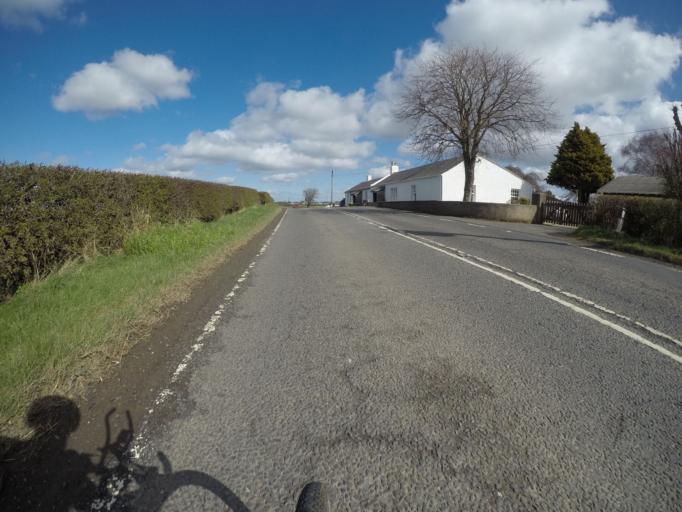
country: GB
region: Scotland
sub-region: East Ayrshire
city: Crosshouse
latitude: 55.5892
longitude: -4.5547
